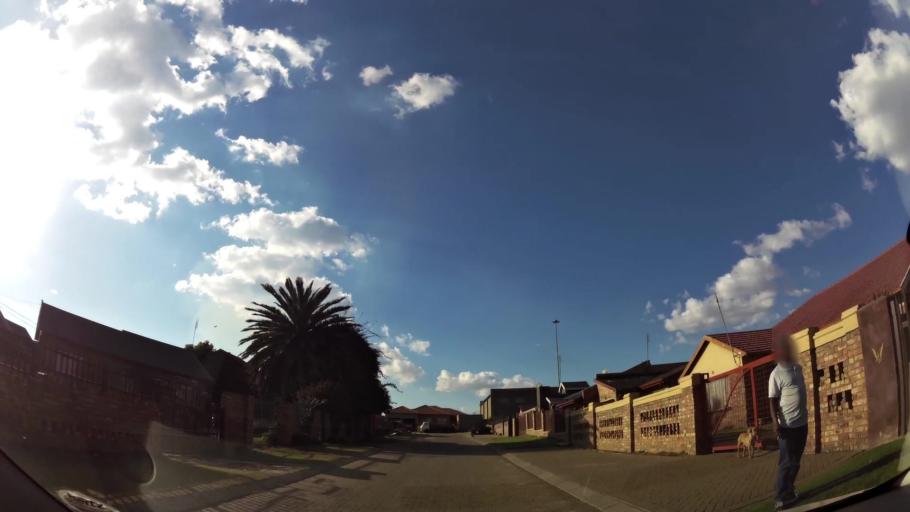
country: ZA
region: Mpumalanga
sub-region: Nkangala District Municipality
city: Witbank
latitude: -25.8715
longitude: 29.1845
